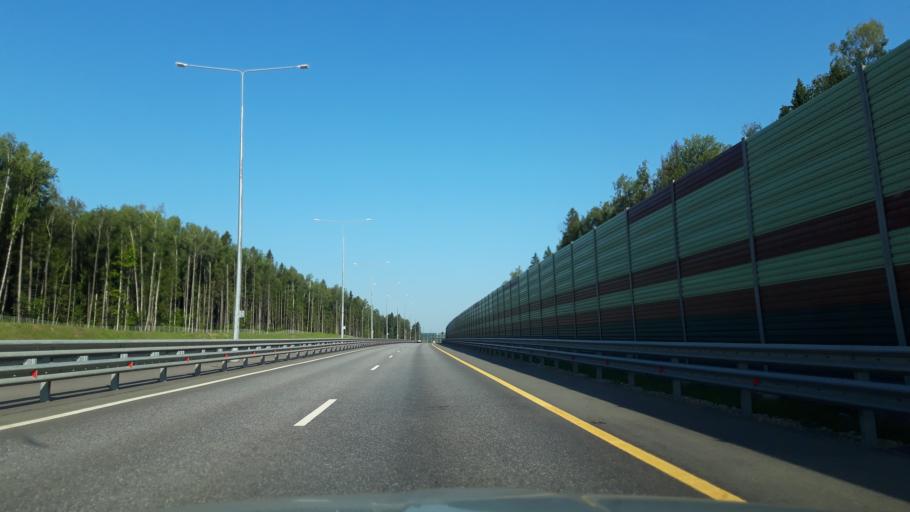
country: RU
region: Moskovskaya
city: Klin
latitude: 56.2220
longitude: 36.7734
